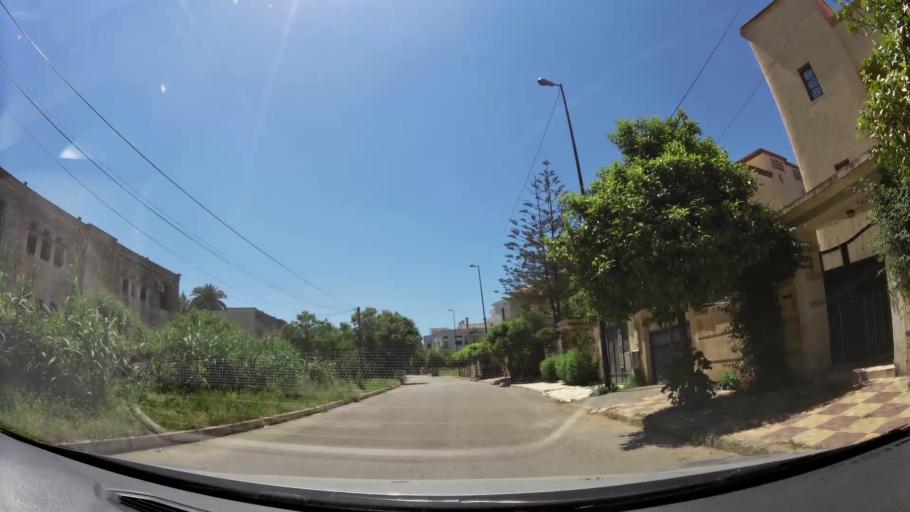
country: MA
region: Meknes-Tafilalet
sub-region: Meknes
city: Meknes
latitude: 33.8842
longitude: -5.5379
